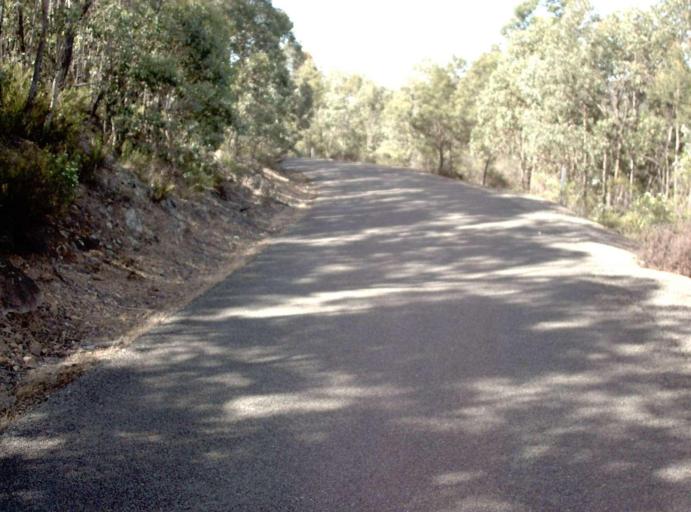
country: AU
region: Victoria
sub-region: East Gippsland
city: Lakes Entrance
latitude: -37.4785
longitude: 148.1242
